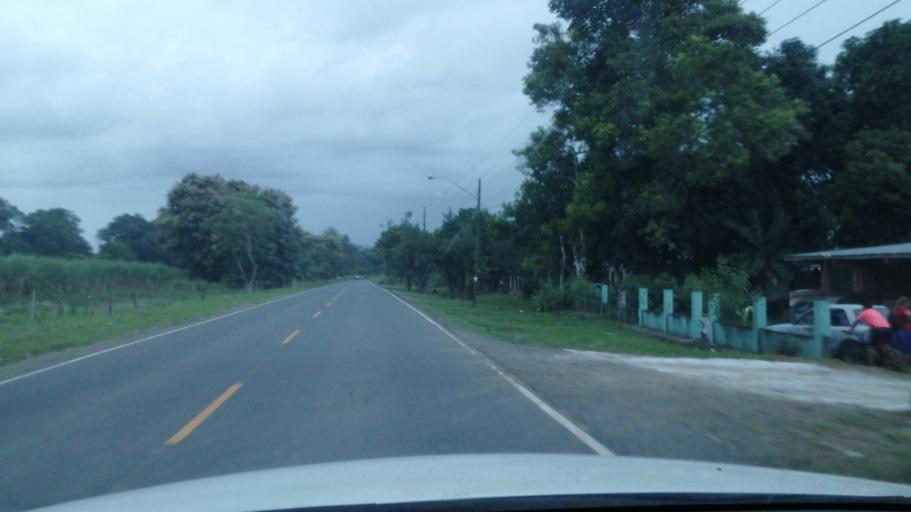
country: PA
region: Chiriqui
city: Alanje
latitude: 8.3950
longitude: -82.4945
